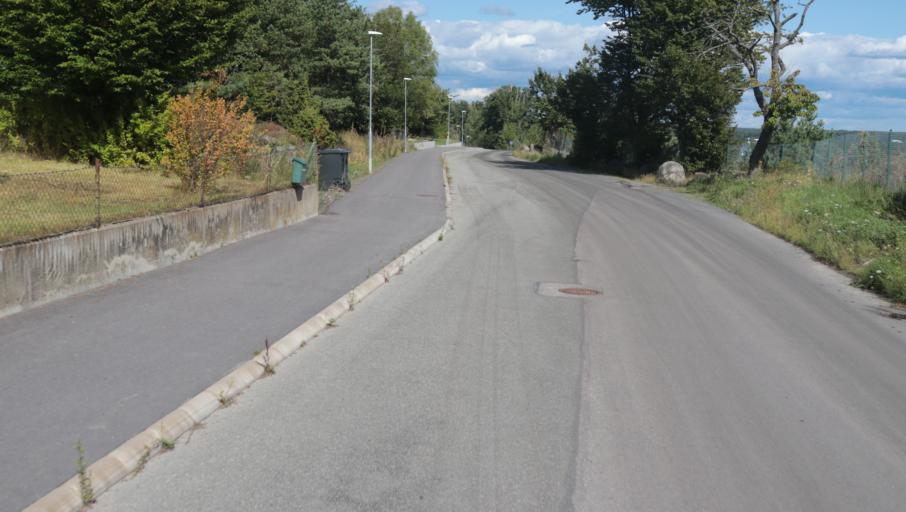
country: SE
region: Blekinge
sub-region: Karlshamns Kommun
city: Karlshamn
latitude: 56.1462
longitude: 14.8466
